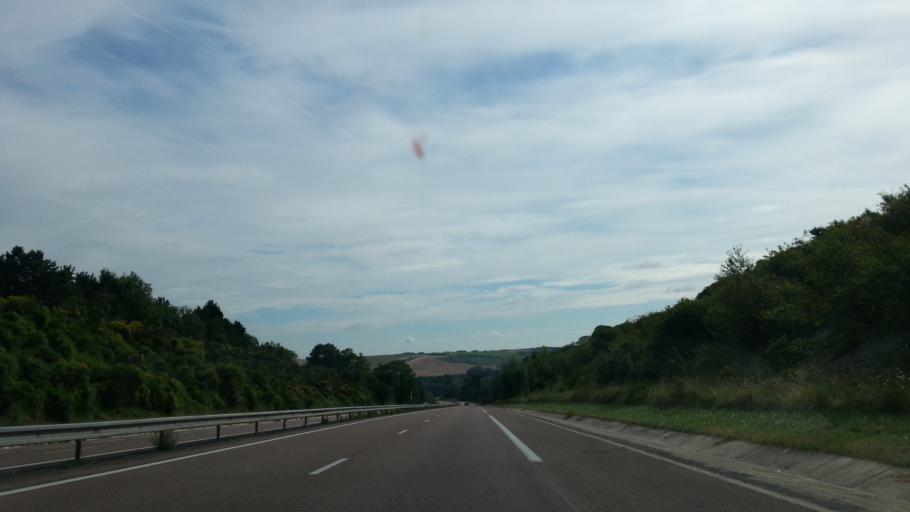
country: FR
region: Champagne-Ardenne
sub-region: Departement de la Marne
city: Jonchery-sur-Vesle
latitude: 49.2157
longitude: 3.8020
